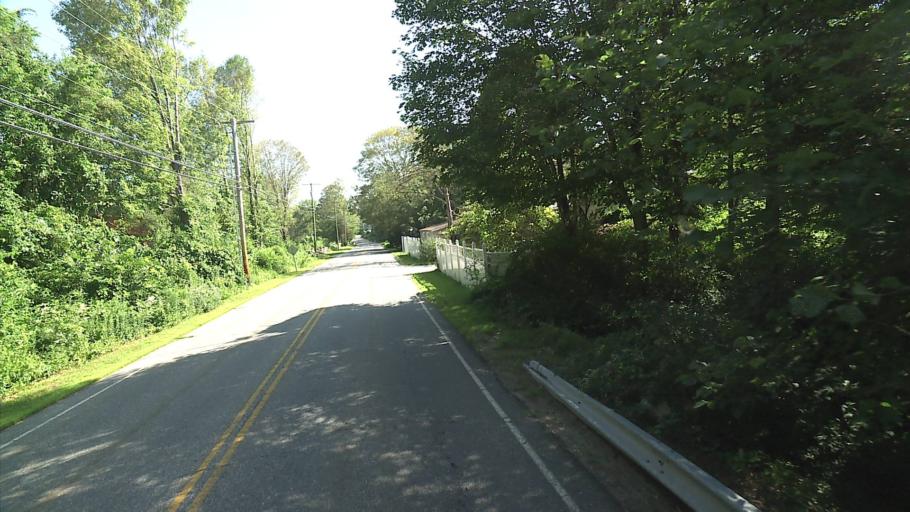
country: US
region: Connecticut
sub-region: New London County
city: Montville Center
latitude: 41.5470
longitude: -72.1732
